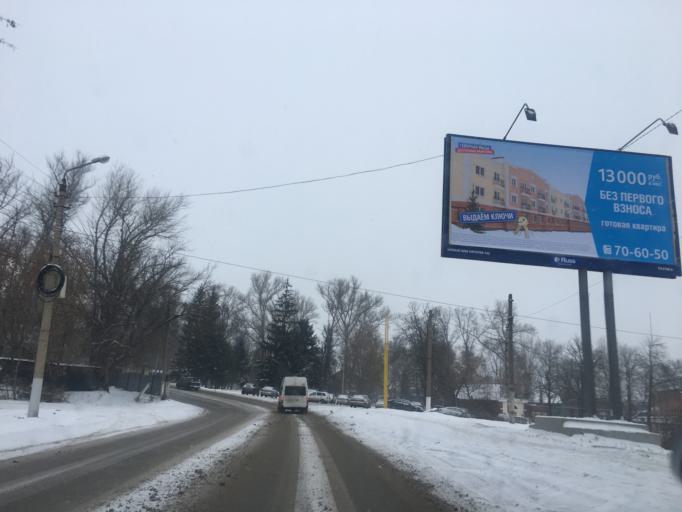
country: RU
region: Tula
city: Tula
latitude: 54.1938
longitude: 37.5670
